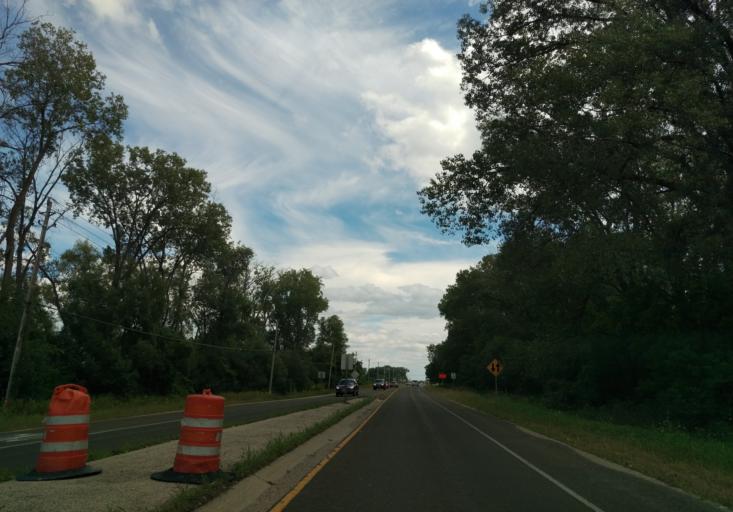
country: US
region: Wisconsin
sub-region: Dane County
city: Waunakee
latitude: 43.1478
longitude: -89.4317
